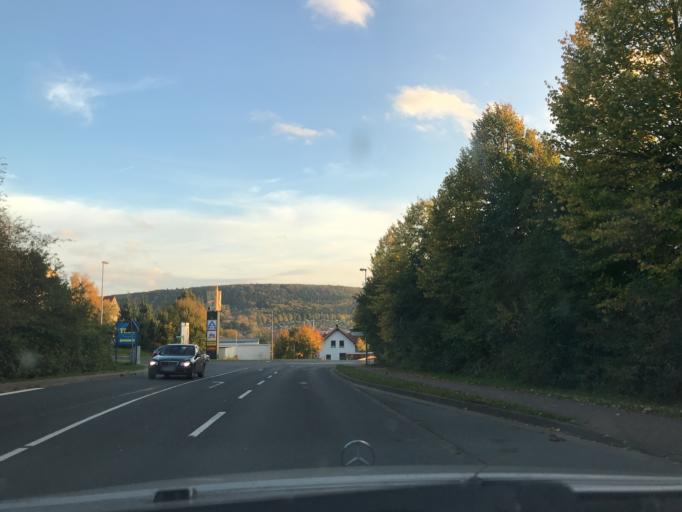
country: DE
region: Thuringia
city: Heilbad Heiligenstadt
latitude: 51.3859
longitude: 10.1313
